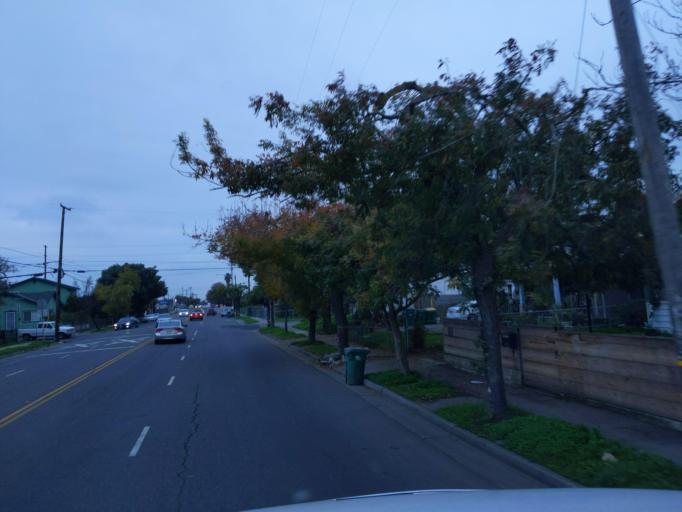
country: US
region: California
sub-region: San Joaquin County
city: Stockton
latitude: 37.9469
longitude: -121.2719
